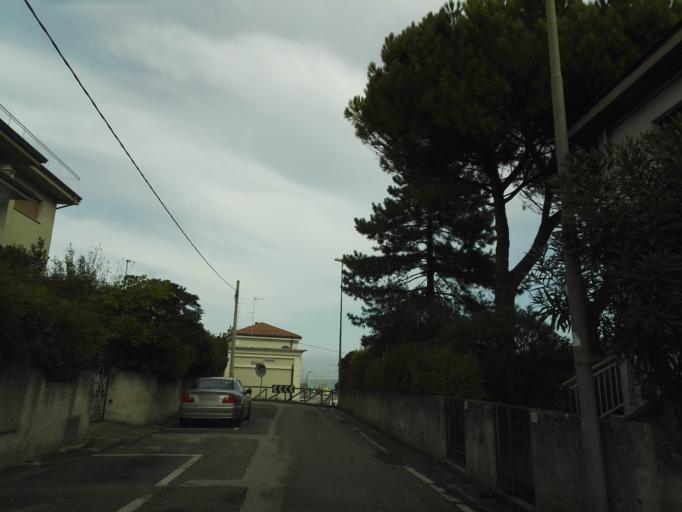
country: IT
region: The Marches
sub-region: Provincia di Pesaro e Urbino
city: Marotta
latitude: 43.7669
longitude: 13.1392
